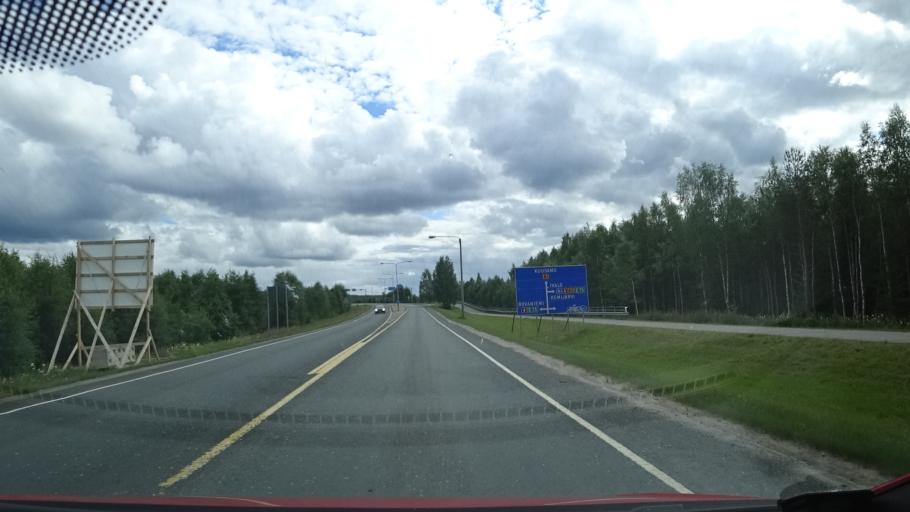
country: FI
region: Lapland
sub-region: Rovaniemi
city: Rovaniemi
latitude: 66.5217
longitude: 25.7463
